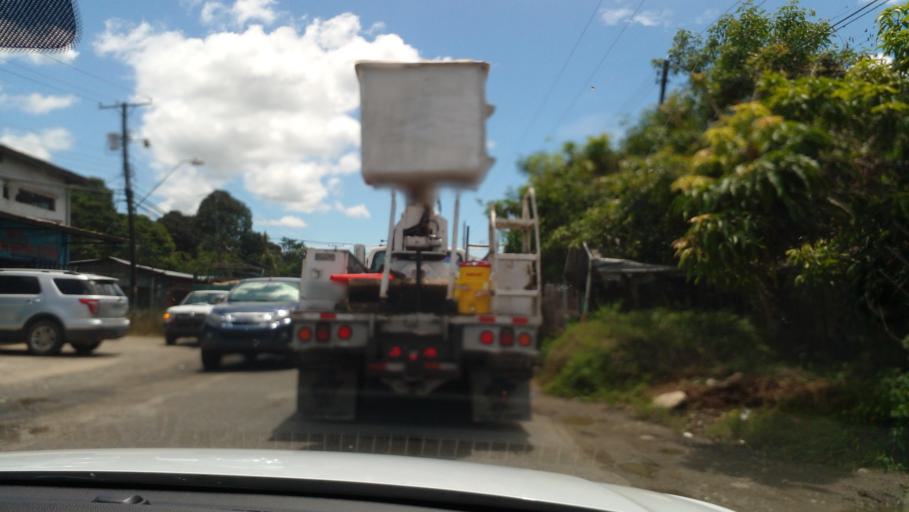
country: PA
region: Bocas del Toro
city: Almirante
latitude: 9.2936
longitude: -82.4065
